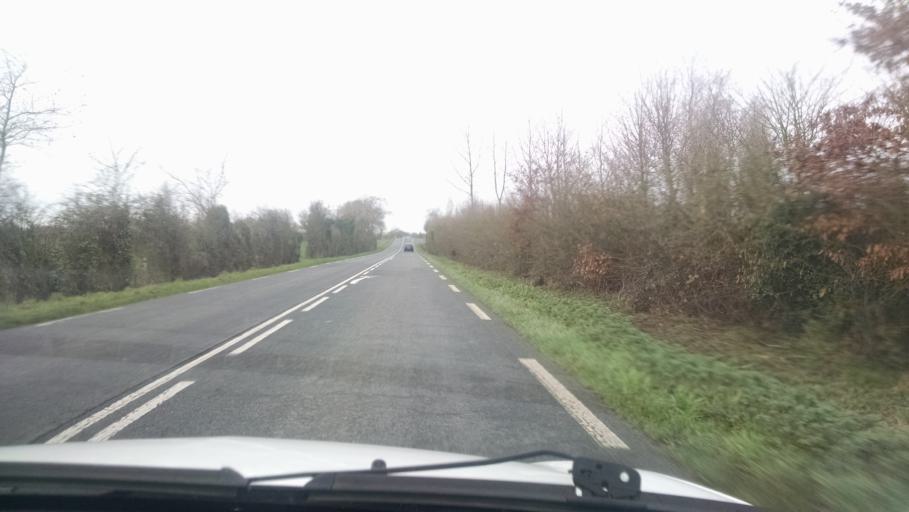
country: FR
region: Pays de la Loire
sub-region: Departement de la Loire-Atlantique
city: Boussay
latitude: 47.0494
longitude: -1.1530
